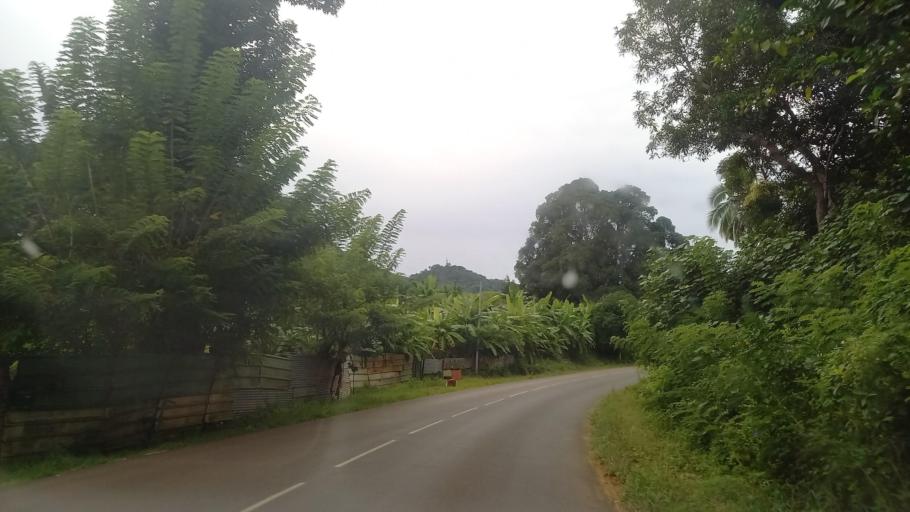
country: YT
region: Boueni
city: Boueni
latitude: -12.9212
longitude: 45.1022
